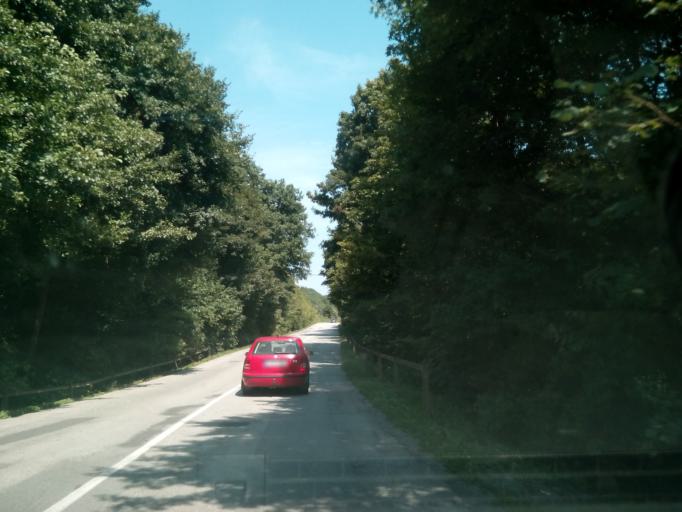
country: SK
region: Kosicky
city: Kosice
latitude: 48.7768
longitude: 21.2388
